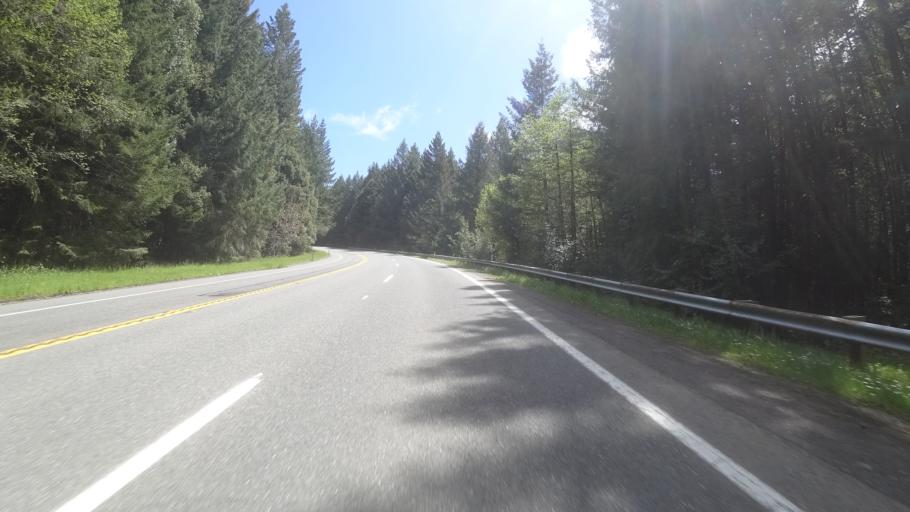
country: US
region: California
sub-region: Humboldt County
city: Blue Lake
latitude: 40.9474
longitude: -123.8927
